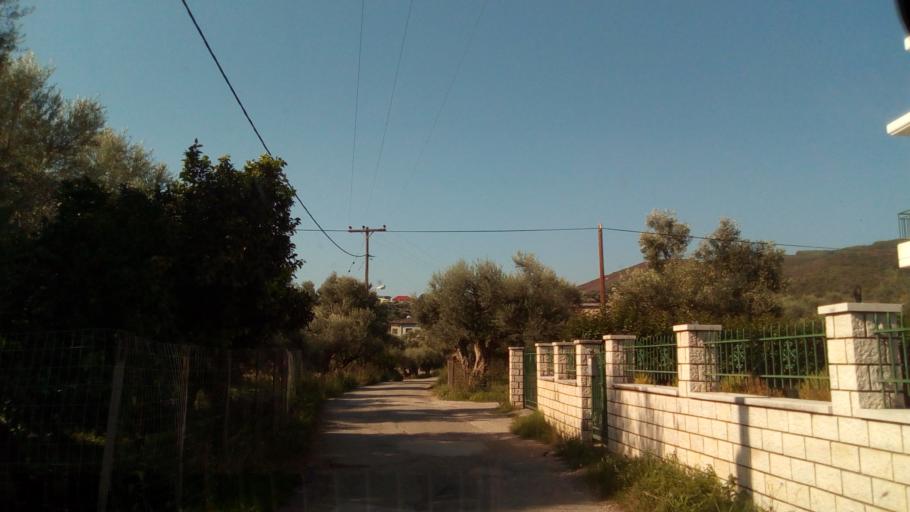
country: GR
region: West Greece
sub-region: Nomos Aitolias kai Akarnanias
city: Nafpaktos
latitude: 38.3833
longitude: 21.8000
